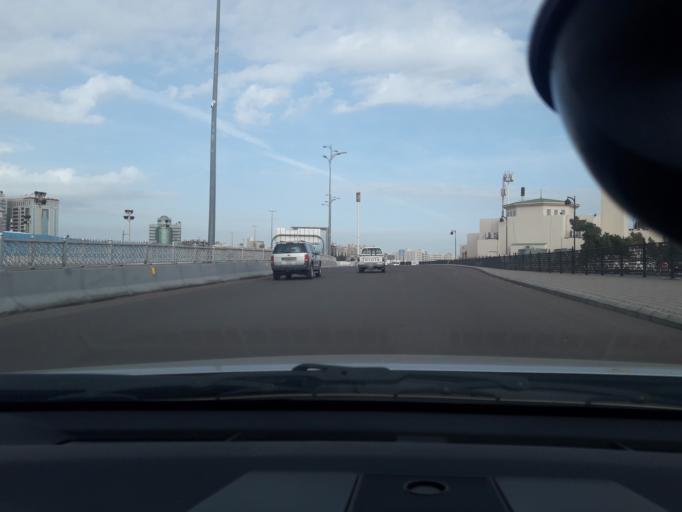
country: SA
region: Al Madinah al Munawwarah
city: Medina
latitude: 24.4709
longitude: 39.6187
